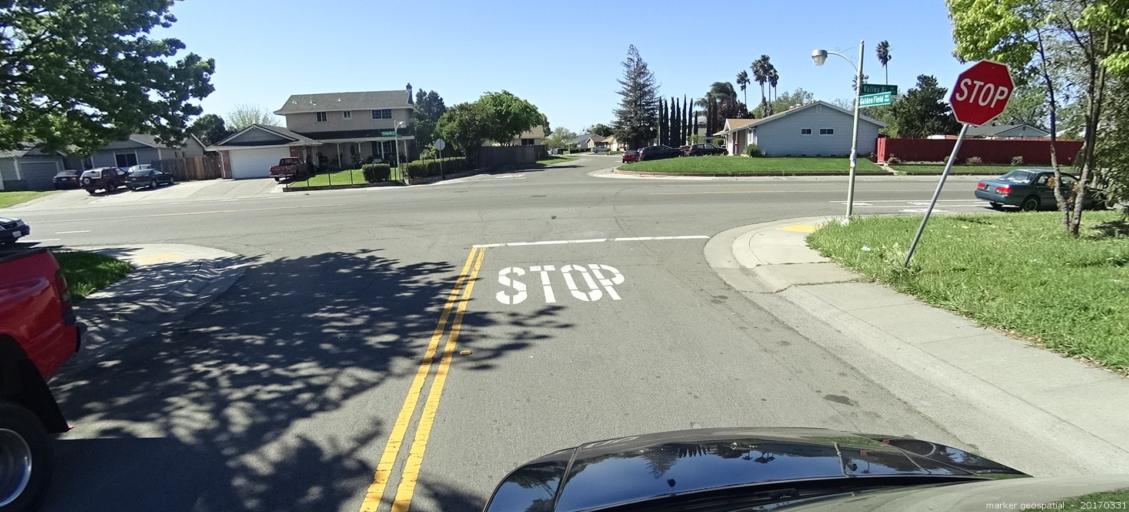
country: US
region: California
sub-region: Sacramento County
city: Florin
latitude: 38.4640
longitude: -121.4338
